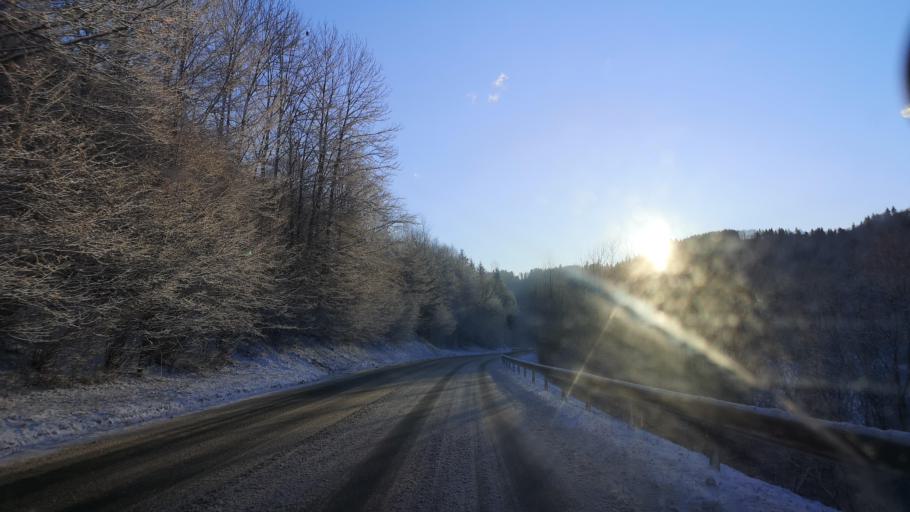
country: SK
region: Banskobystricky
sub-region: Okres Banska Bystrica
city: Brezno
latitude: 48.8226
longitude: 19.6993
